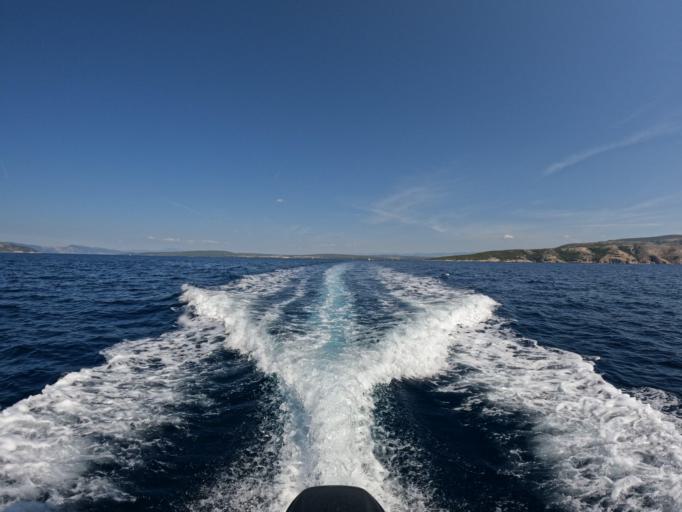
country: HR
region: Primorsko-Goranska
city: Punat
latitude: 44.9557
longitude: 14.6112
